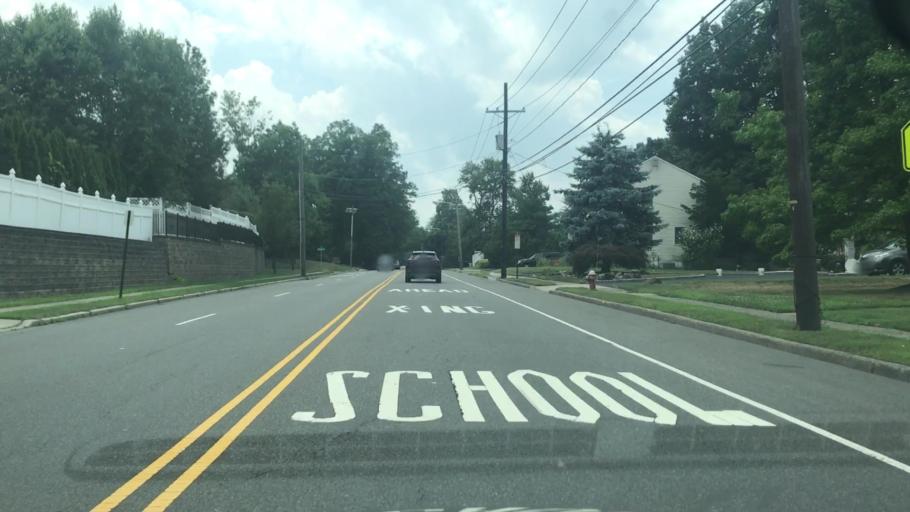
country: US
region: New Jersey
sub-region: Union County
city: Clark
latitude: 40.6159
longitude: -74.3247
